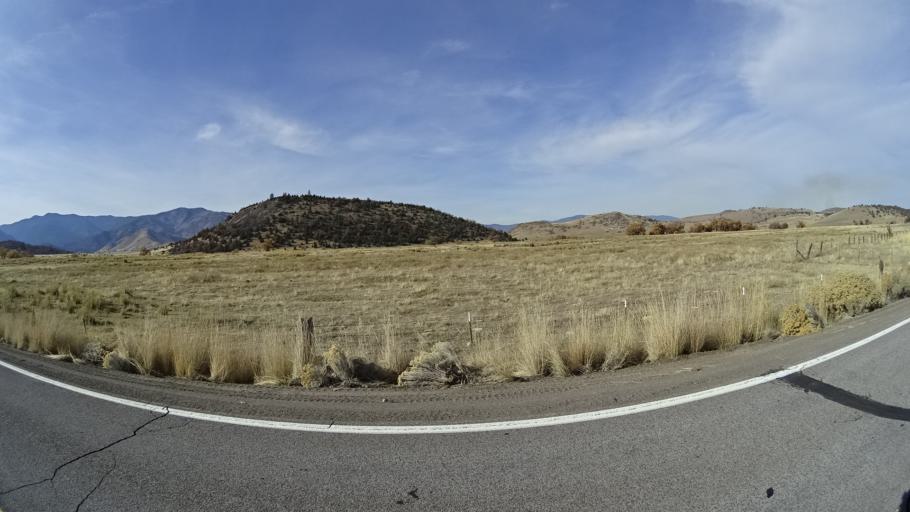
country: US
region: California
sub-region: Siskiyou County
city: Weed
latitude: 41.4828
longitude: -122.4098
